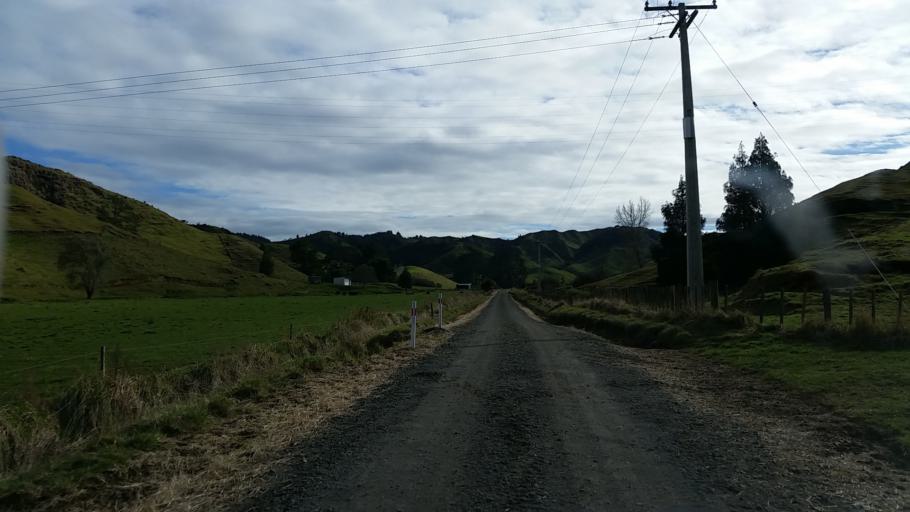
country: NZ
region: Taranaki
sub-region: South Taranaki District
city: Eltham
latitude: -39.2330
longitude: 174.5678
